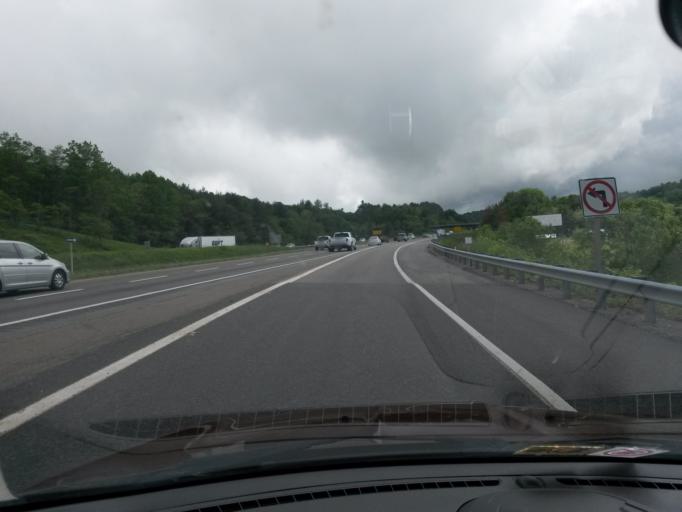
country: US
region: Virginia
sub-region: Carroll County
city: Cana
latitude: 36.6710
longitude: -80.7091
